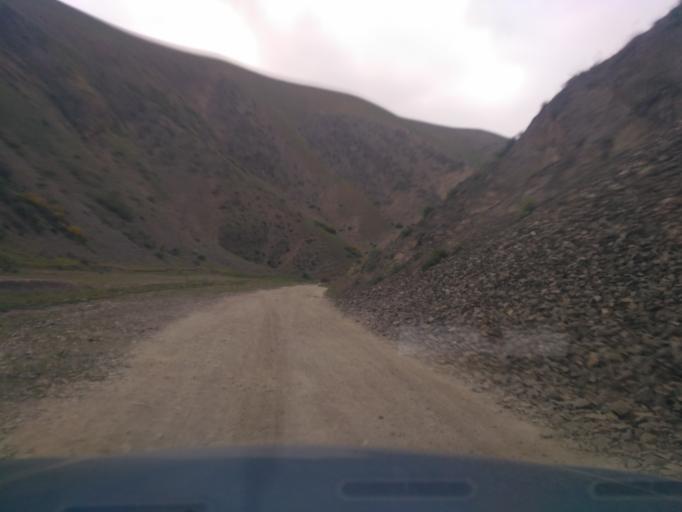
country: UZ
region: Jizzax
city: Zomin
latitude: 39.8547
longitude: 68.3912
